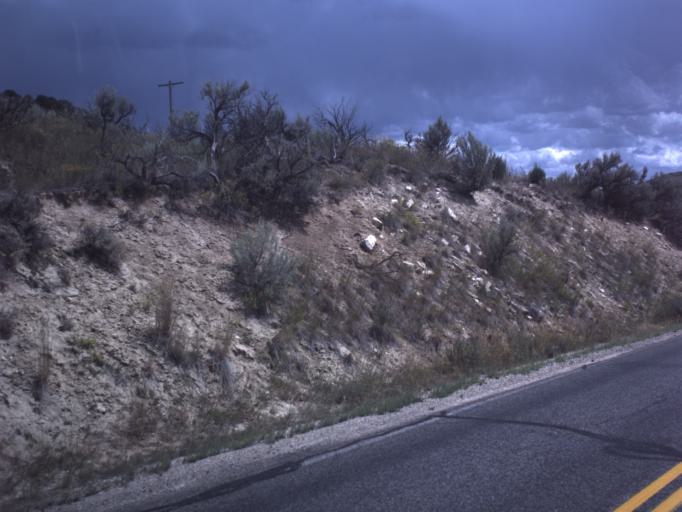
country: US
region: Utah
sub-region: Summit County
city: Oakley
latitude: 40.7577
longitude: -111.3743
